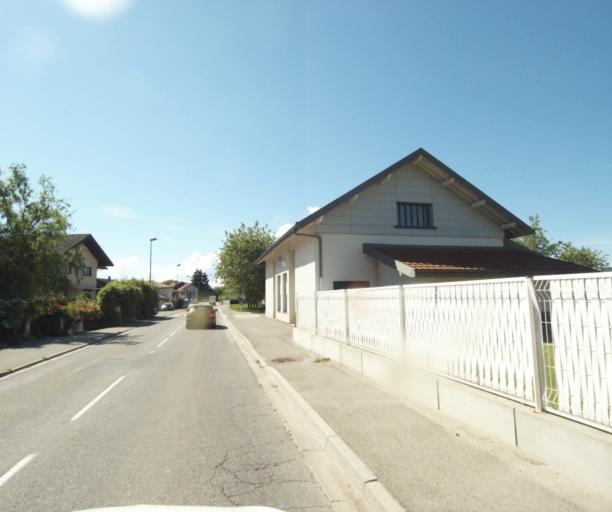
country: FR
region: Rhone-Alpes
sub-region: Departement de la Haute-Savoie
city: Bons-en-Chablais
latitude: 46.2700
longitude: 6.3646
